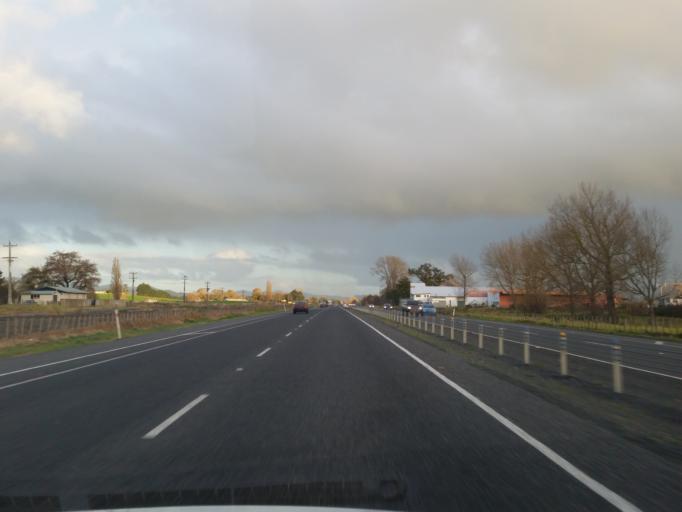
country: NZ
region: Waikato
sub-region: Waikato District
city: Te Kauwhata
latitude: -37.4621
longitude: 175.1563
